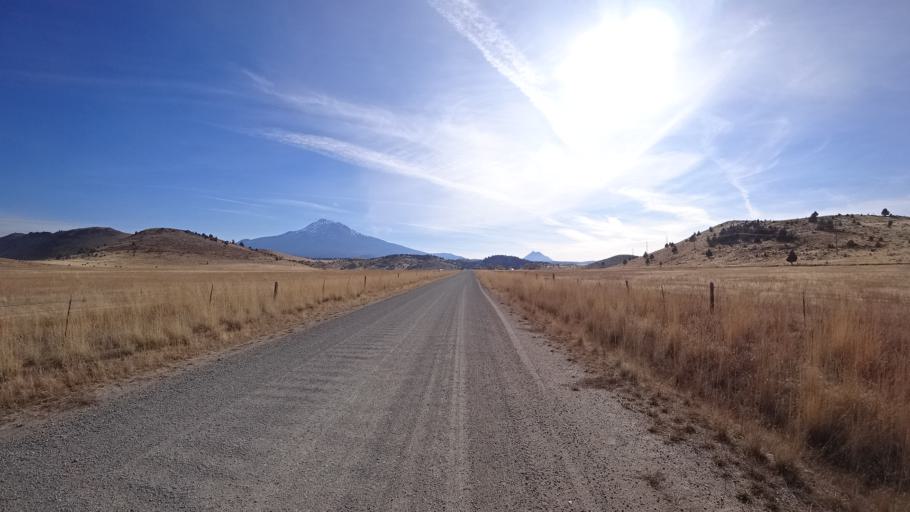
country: US
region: California
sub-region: Siskiyou County
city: Weed
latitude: 41.5084
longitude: -122.4616
